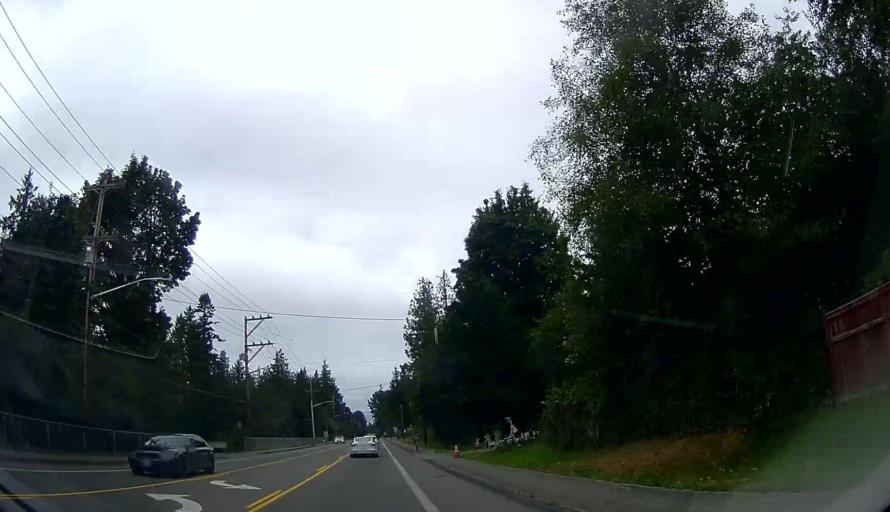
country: US
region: Washington
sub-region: Snohomish County
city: Marysville
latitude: 48.0436
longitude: -122.2201
